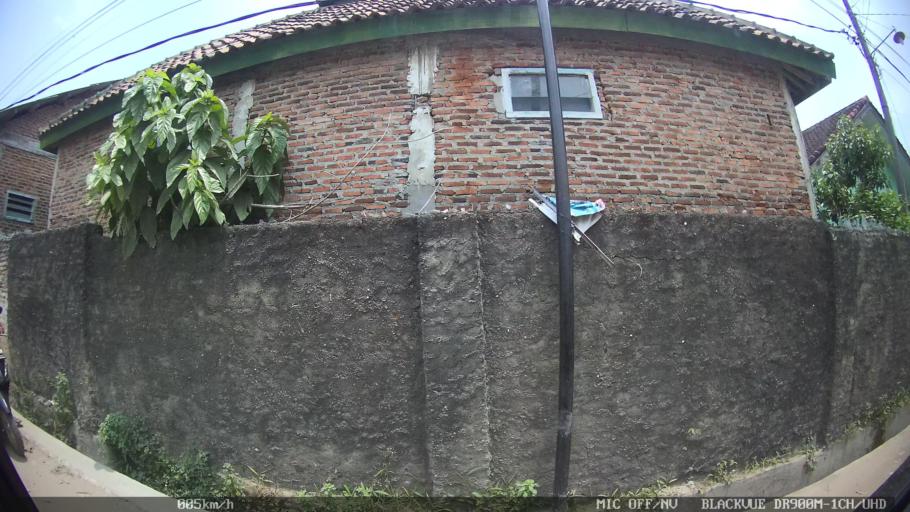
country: ID
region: Lampung
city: Kedaton
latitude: -5.3952
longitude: 105.2998
